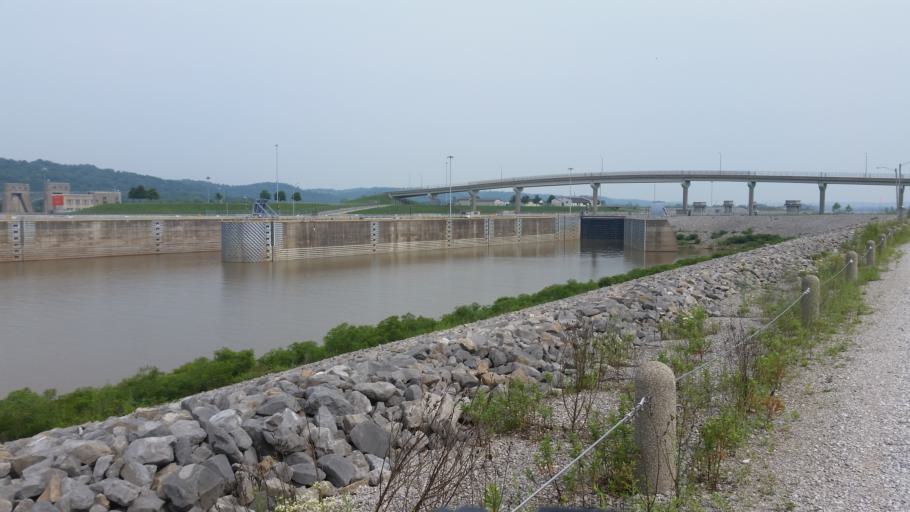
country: US
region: Ohio
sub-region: Gallia County
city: Gallipolis
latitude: 38.6789
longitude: -82.1831
